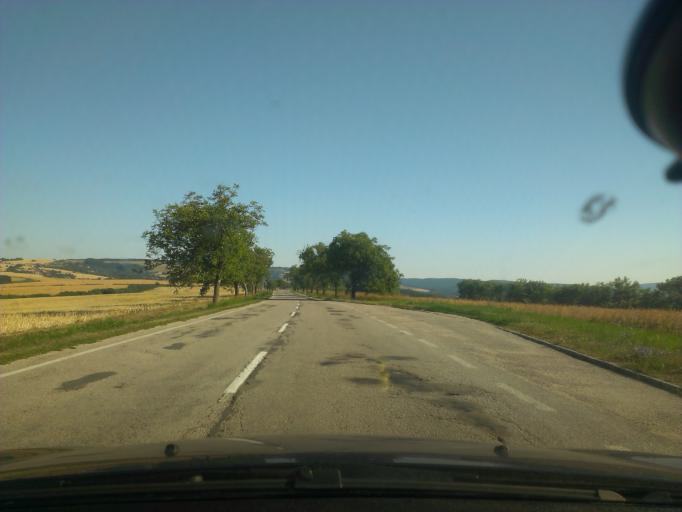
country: SK
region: Trenciansky
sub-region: Okres Myjava
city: Myjava
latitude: 48.7607
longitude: 17.5582
